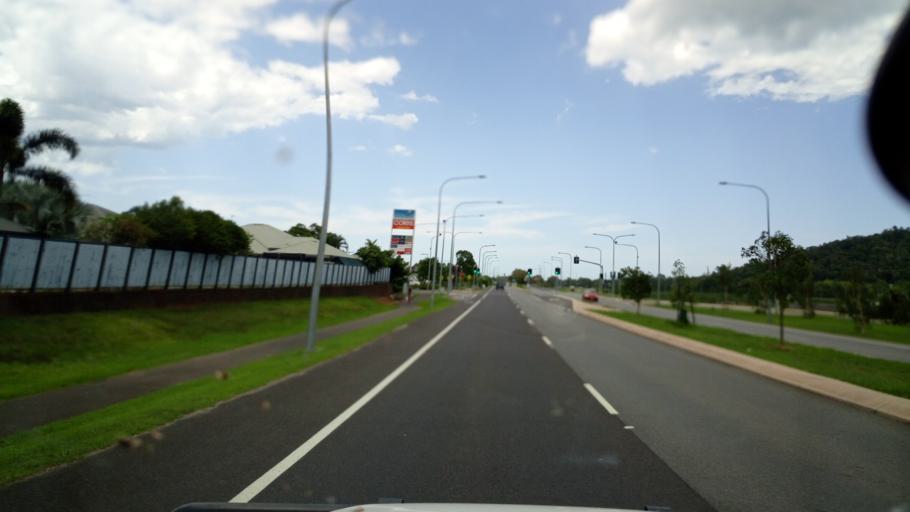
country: AU
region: Queensland
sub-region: Cairns
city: Redlynch
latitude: -16.8991
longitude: 145.6997
